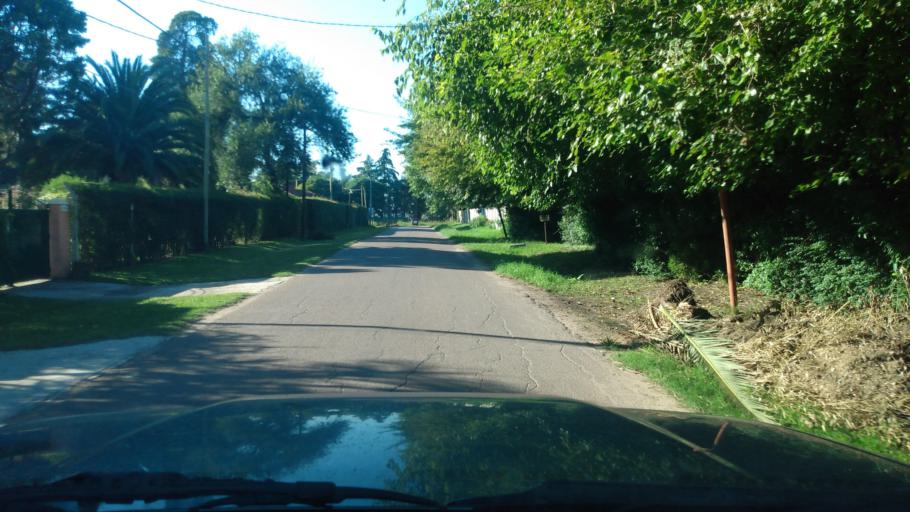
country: AR
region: Buenos Aires
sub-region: Partido de Lujan
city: Lujan
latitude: -34.5478
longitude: -59.1391
